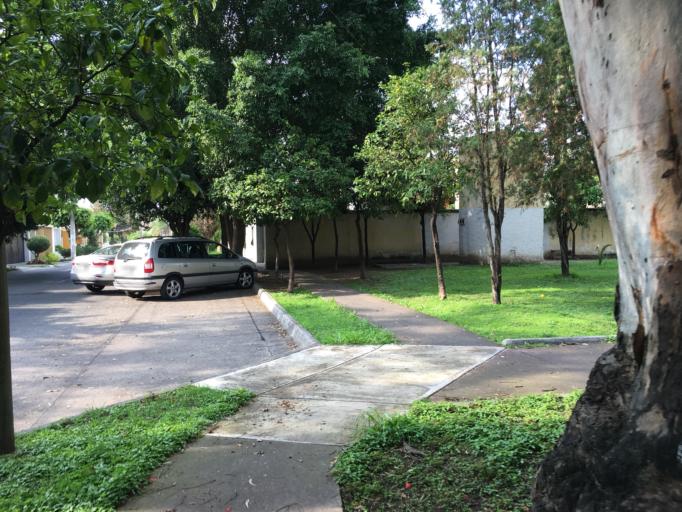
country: MX
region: Jalisco
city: Guadalajara
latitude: 20.6498
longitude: -103.3944
